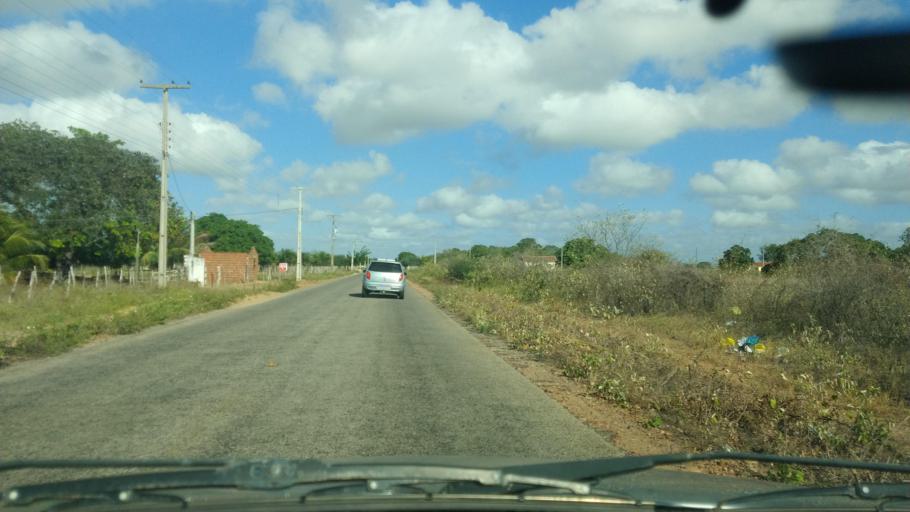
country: BR
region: Rio Grande do Norte
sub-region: Sao Paulo Do Potengi
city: Sao Paulo do Potengi
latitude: -5.9156
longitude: -35.7139
